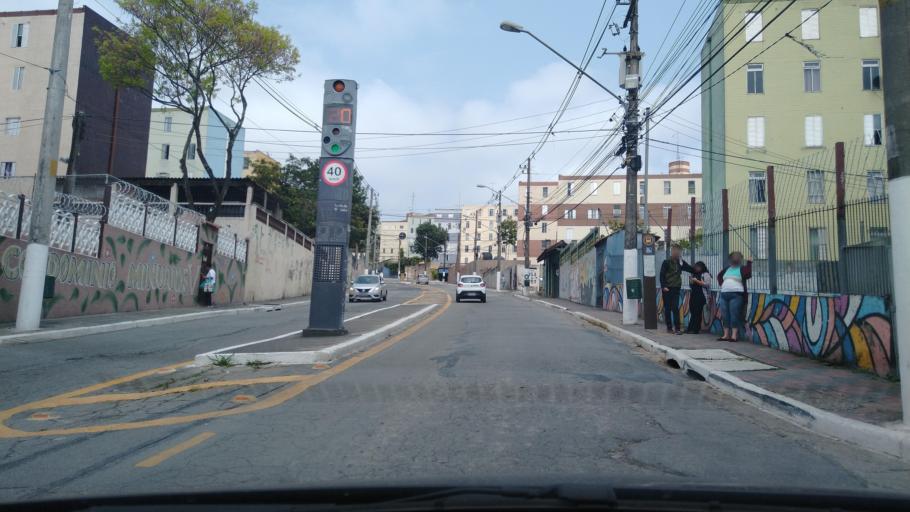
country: BR
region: Sao Paulo
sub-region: Caieiras
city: Caieiras
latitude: -23.4420
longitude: -46.7129
